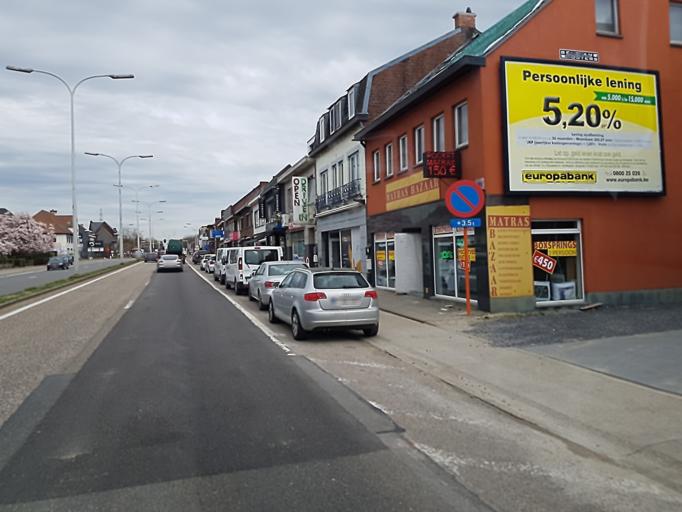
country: BE
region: Flanders
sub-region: Provincie Limburg
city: Houthalen
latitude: 51.0291
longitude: 5.3760
